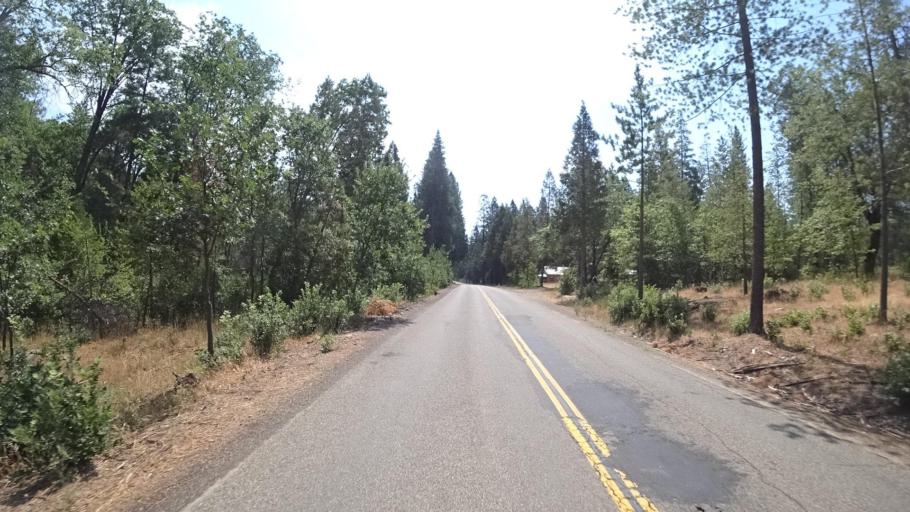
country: US
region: California
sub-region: Mariposa County
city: Midpines
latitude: 37.7237
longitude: -120.1033
